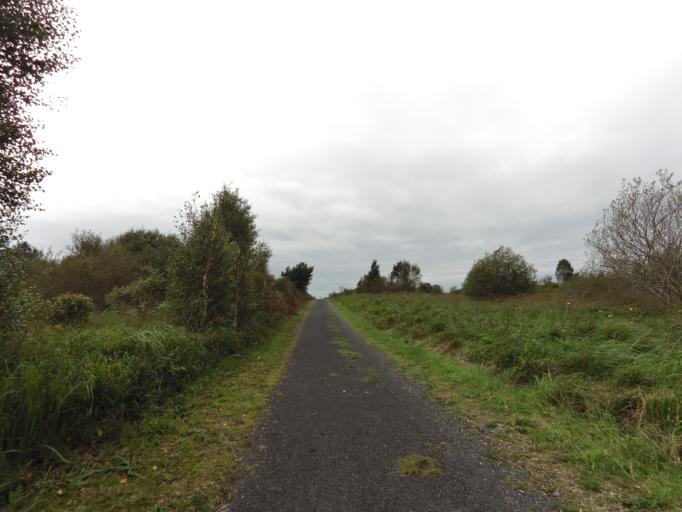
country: IE
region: Leinster
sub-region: Uibh Fhaili
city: Ferbane
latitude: 53.2134
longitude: -7.7642
